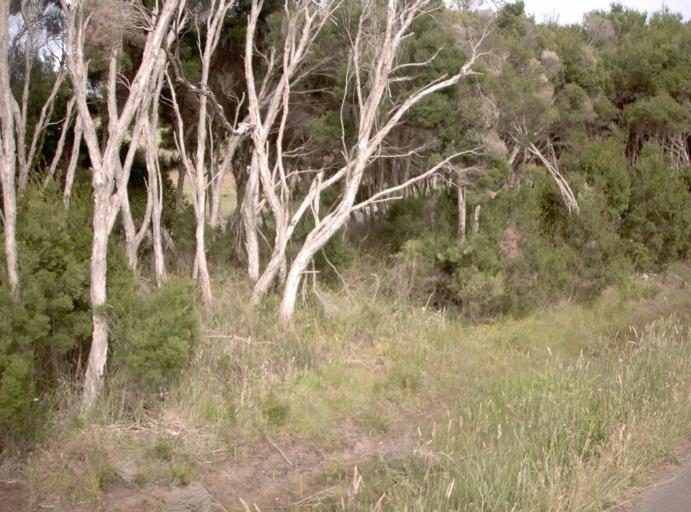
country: AU
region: Victoria
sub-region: Bass Coast
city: Phillip Island
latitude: -38.4901
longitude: 145.2654
